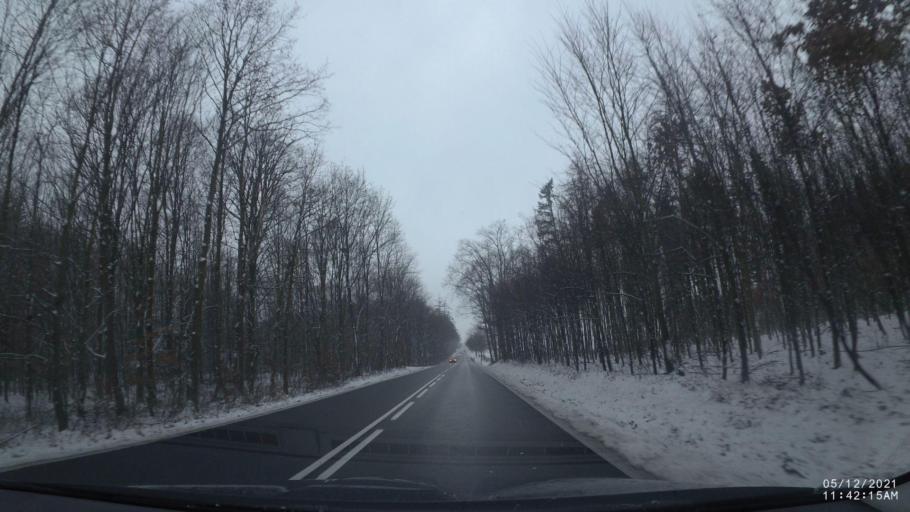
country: CZ
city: Dobruska
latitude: 50.2762
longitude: 16.1903
